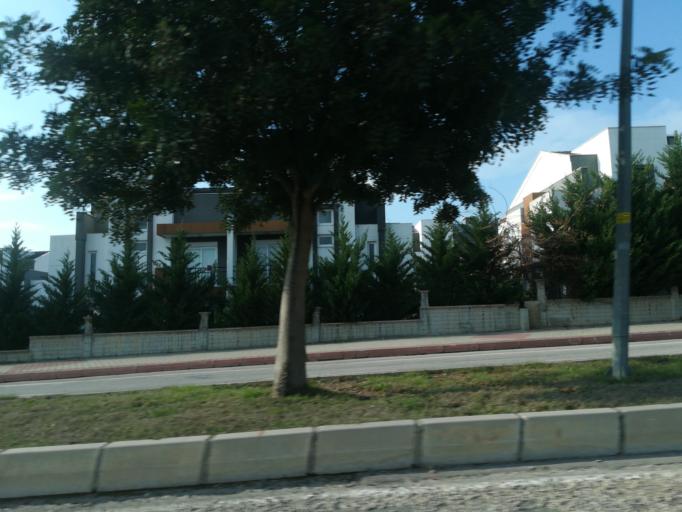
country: TR
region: Adana
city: Adana
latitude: 37.0750
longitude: 35.3860
